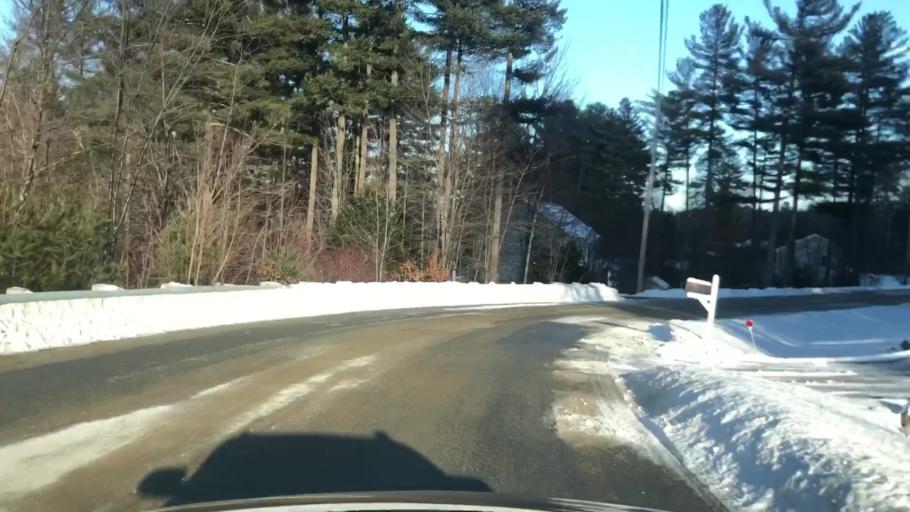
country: US
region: New Hampshire
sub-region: Hillsborough County
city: Milford
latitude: 42.8153
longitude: -71.6699
